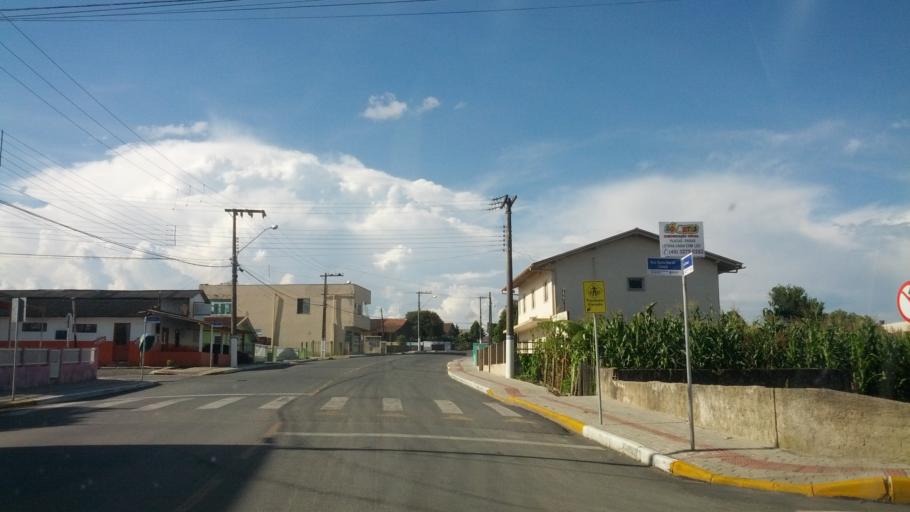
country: BR
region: Santa Catarina
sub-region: Otacilio Costa
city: Otacilio Costa
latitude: -27.4985
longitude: -50.1239
